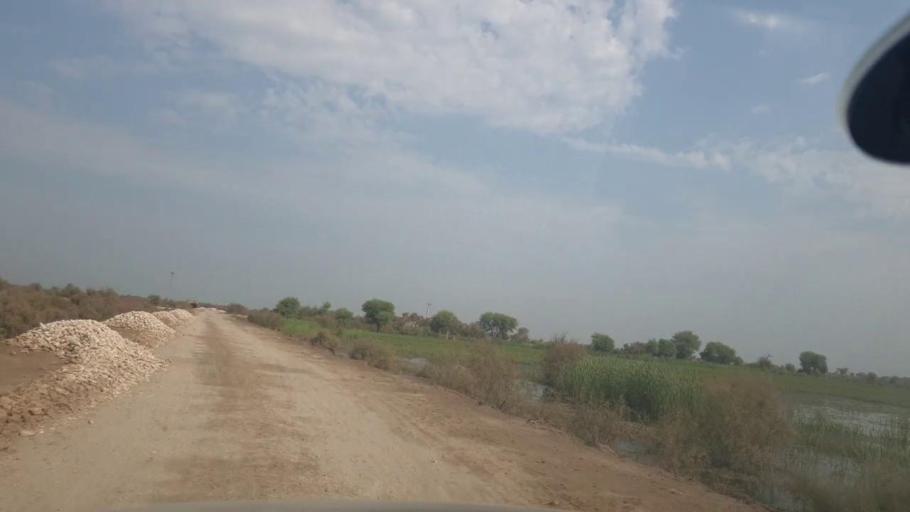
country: PK
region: Balochistan
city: Mehrabpur
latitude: 28.0882
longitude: 68.0973
